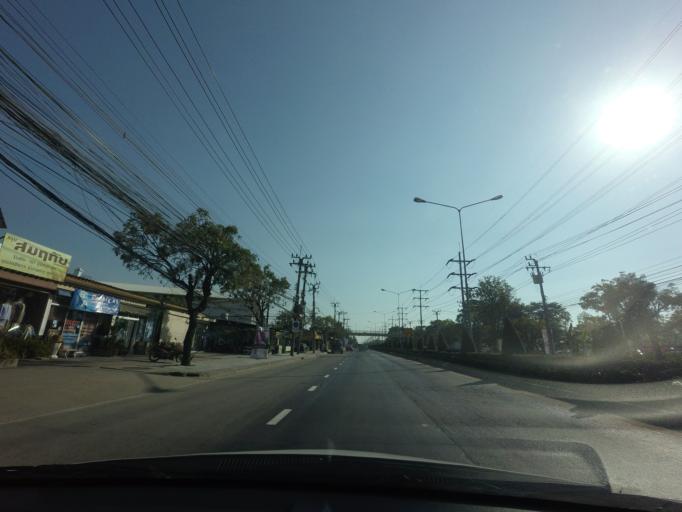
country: TH
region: Bangkok
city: Nong Chok
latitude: 13.8436
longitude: 100.8567
